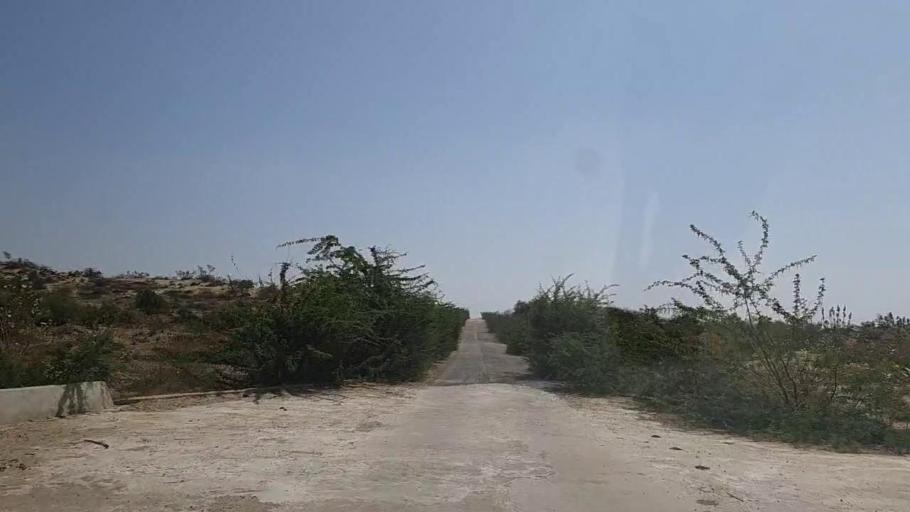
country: PK
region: Sindh
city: Diplo
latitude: 24.4978
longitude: 69.4306
